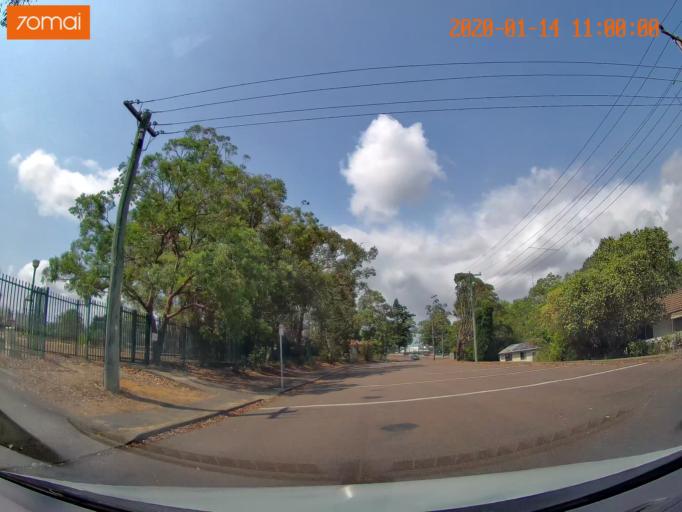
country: AU
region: New South Wales
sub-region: Lake Macquarie Shire
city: Dora Creek
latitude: -33.1037
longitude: 151.4884
